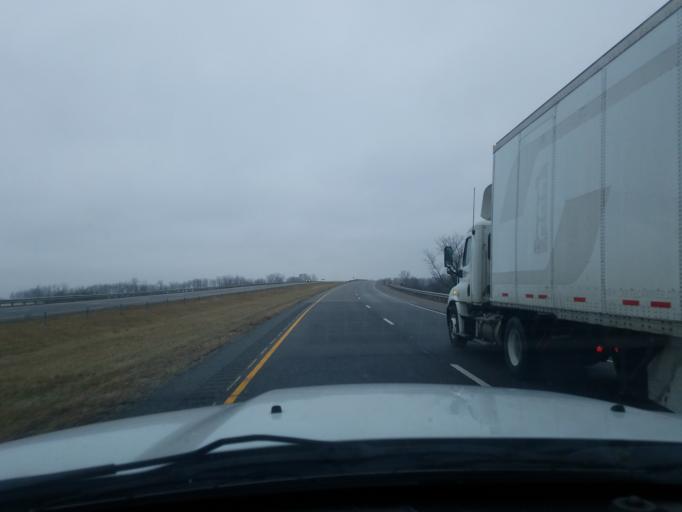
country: US
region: Indiana
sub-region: Grant County
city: Fairmount
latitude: 40.3759
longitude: -85.5564
